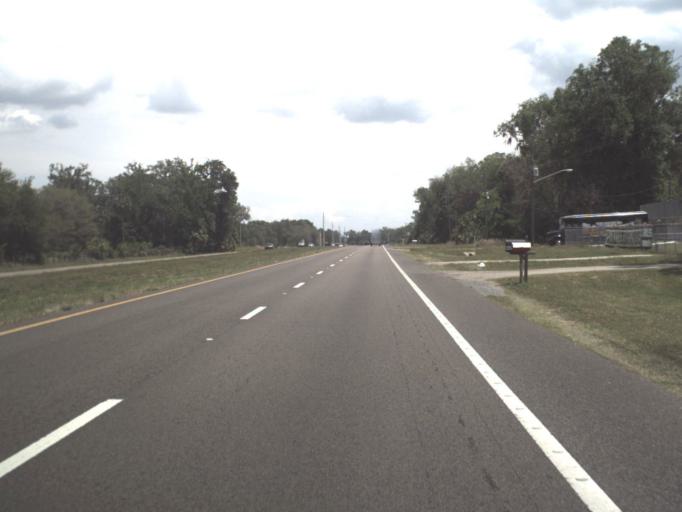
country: US
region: Florida
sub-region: Sumter County
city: Lake Panasoffkee
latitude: 28.8580
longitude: -82.1812
